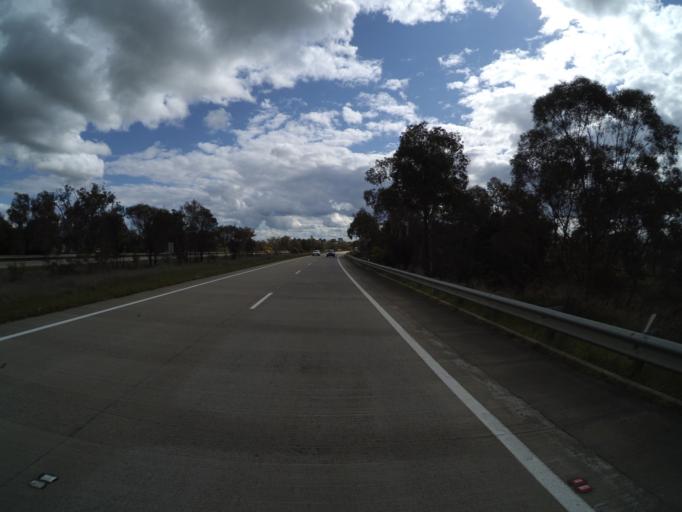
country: AU
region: New South Wales
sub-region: Yass Valley
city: Gundaroo
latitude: -34.7896
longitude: 149.2194
